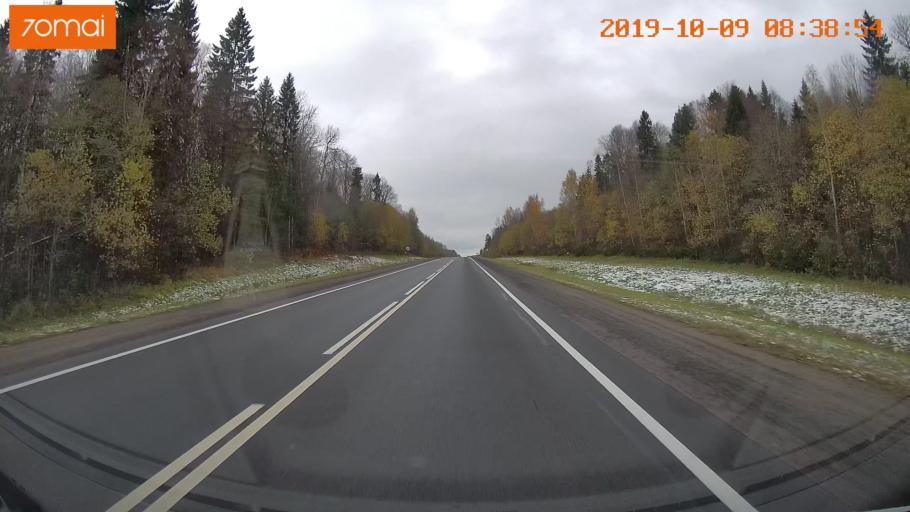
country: RU
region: Vologda
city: Gryazovets
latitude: 58.9634
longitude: 40.1599
